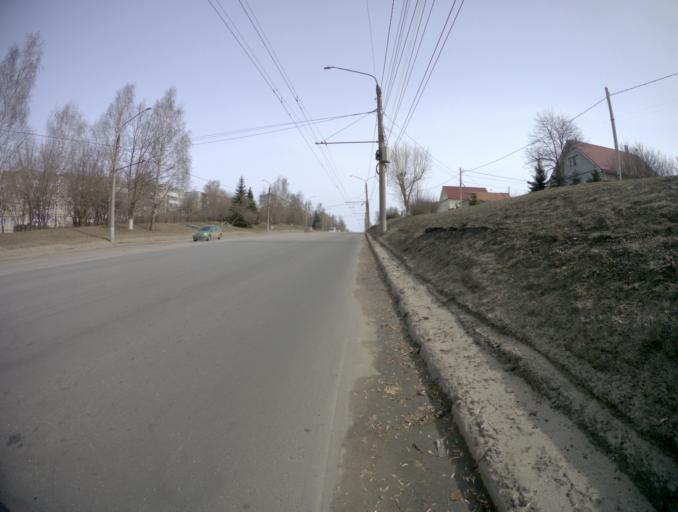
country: RU
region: Vladimir
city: Kommunar
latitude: 56.1555
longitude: 40.4625
